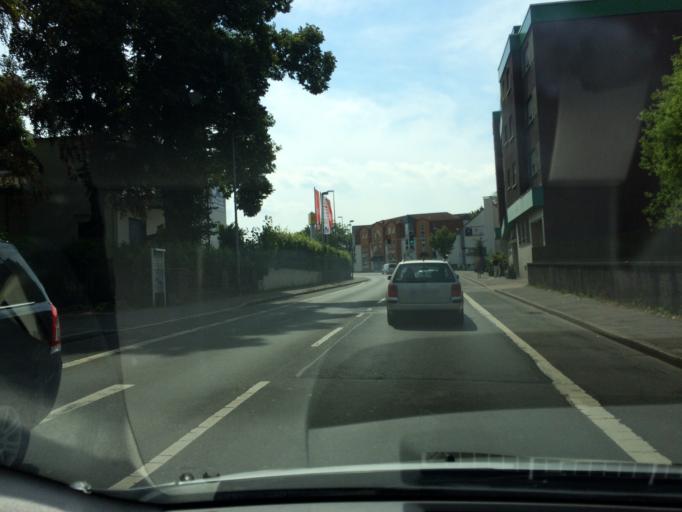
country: DE
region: North Rhine-Westphalia
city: Hemer
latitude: 51.3887
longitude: 7.7647
